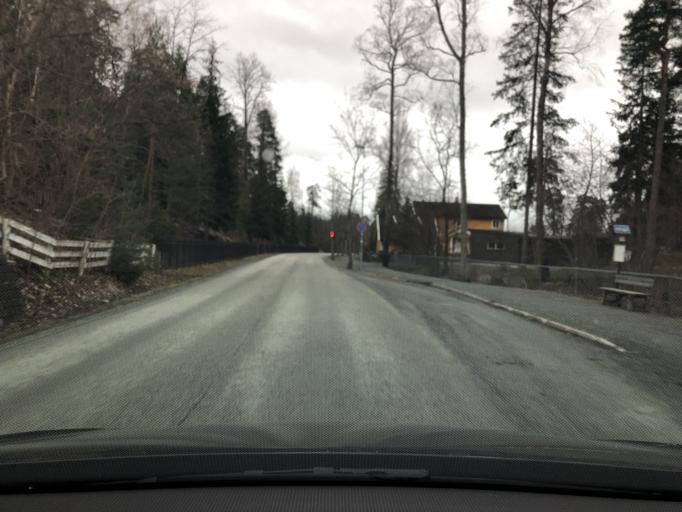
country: NO
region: Akershus
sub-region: Baerum
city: Sandvika
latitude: 59.8632
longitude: 10.5144
